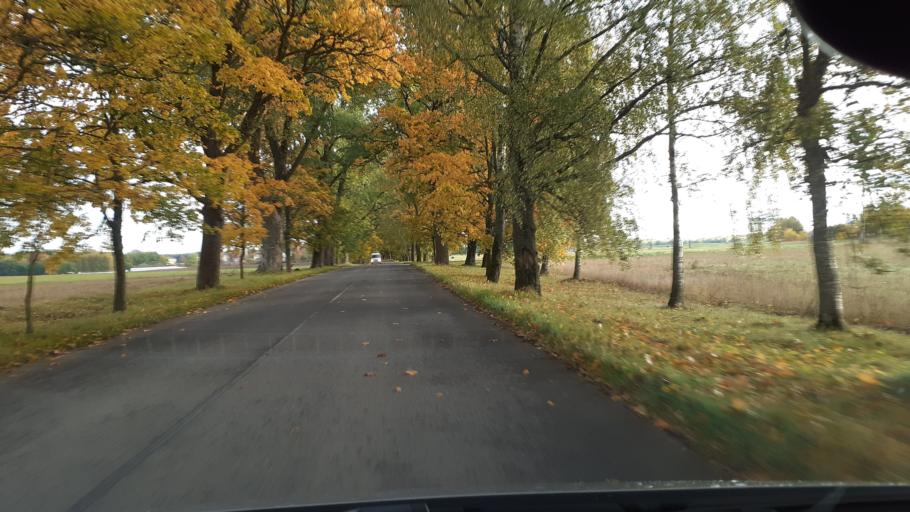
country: LV
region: Kuldigas Rajons
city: Kuldiga
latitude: 57.0089
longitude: 21.8964
